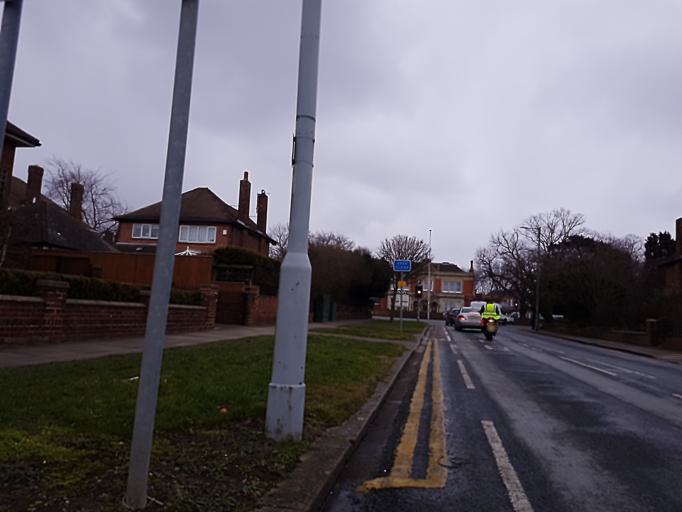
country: GB
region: England
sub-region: North East Lincolnshire
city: Grimbsy
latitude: 53.5565
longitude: -0.0925
